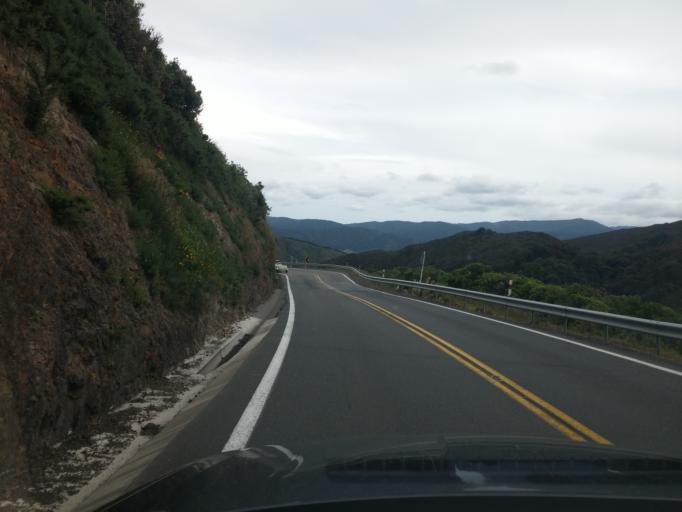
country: NZ
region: Wellington
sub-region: Upper Hutt City
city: Upper Hutt
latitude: -41.1141
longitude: 175.2223
